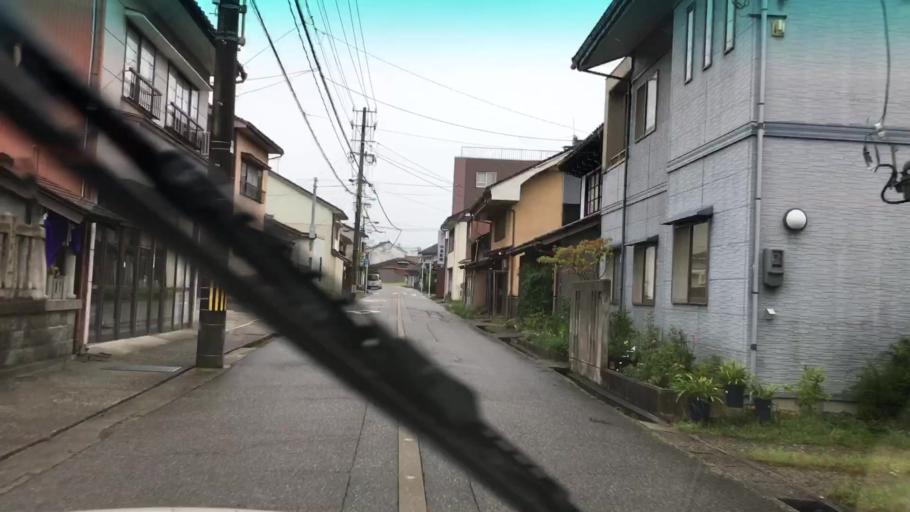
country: JP
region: Toyama
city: Kamiichi
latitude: 36.6595
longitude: 137.3181
